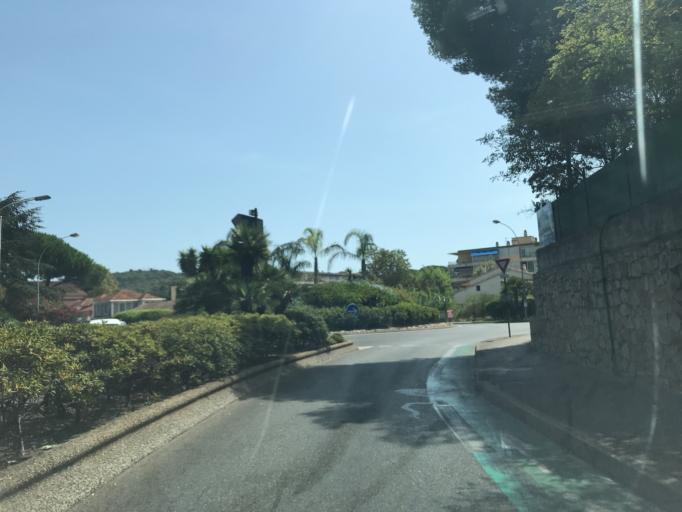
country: FR
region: Provence-Alpes-Cote d'Azur
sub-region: Departement du Var
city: Sanary-sur-Mer
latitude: 43.1194
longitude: 5.8104
